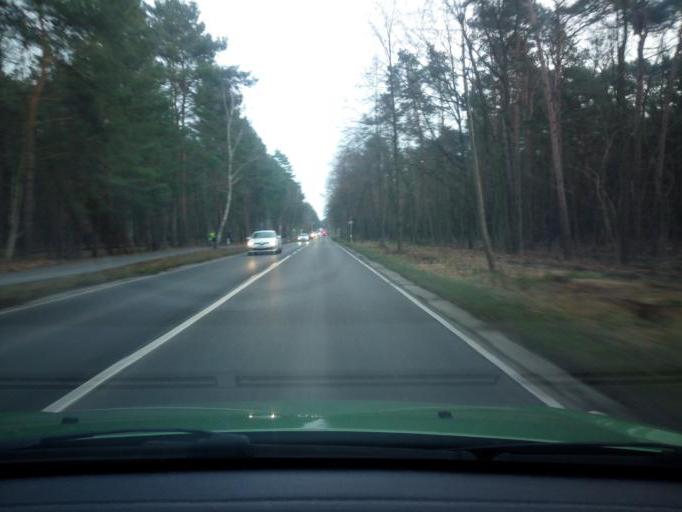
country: DE
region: Berlin
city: Friedrichshagen
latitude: 52.4244
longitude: 13.6251
